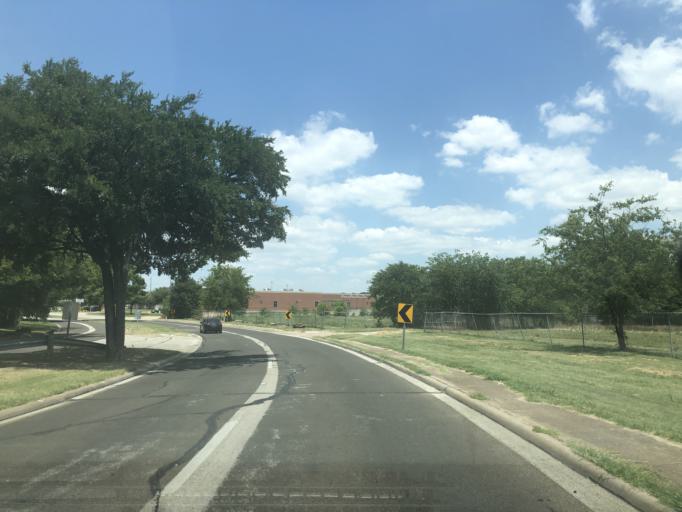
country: US
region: Texas
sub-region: Dallas County
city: Grand Prairie
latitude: 32.7676
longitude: -97.0204
